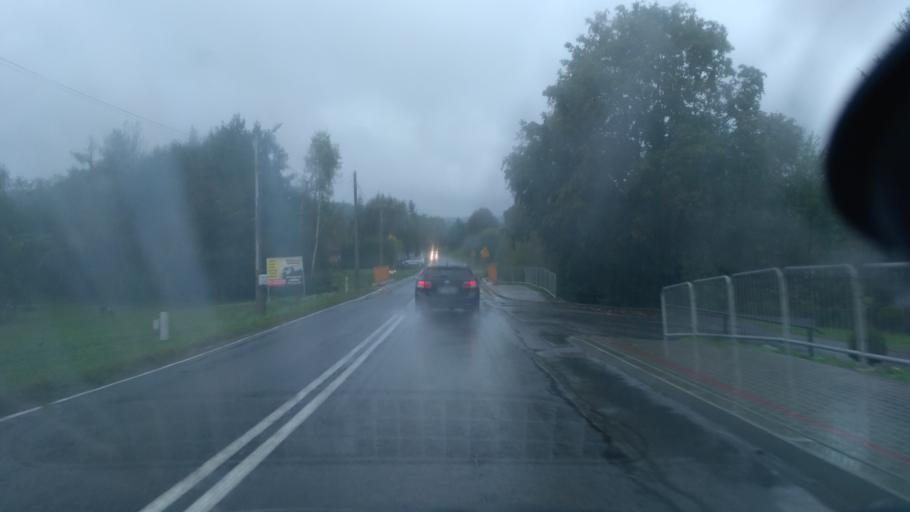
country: PL
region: Subcarpathian Voivodeship
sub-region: Powiat ropczycko-sedziszowski
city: Niedzwiada
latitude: 50.0041
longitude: 21.5580
